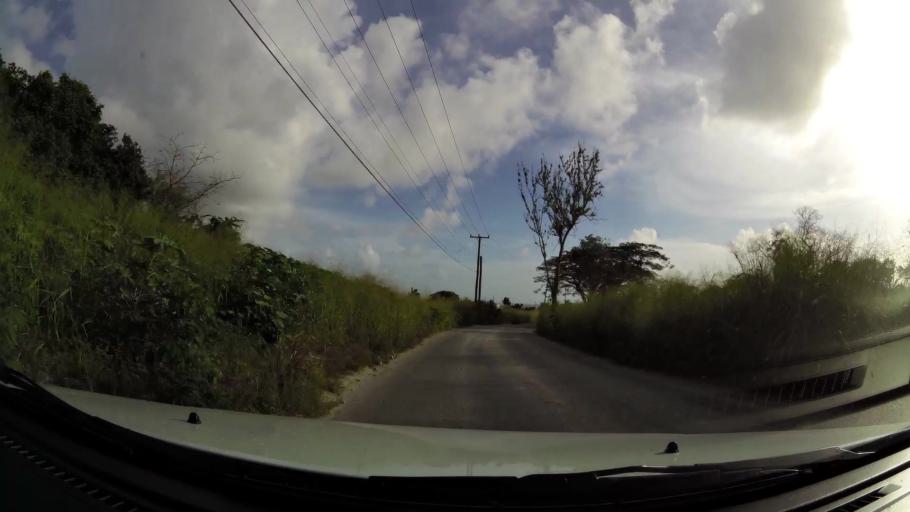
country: BB
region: Christ Church
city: Oistins
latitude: 13.0824
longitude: -59.5498
